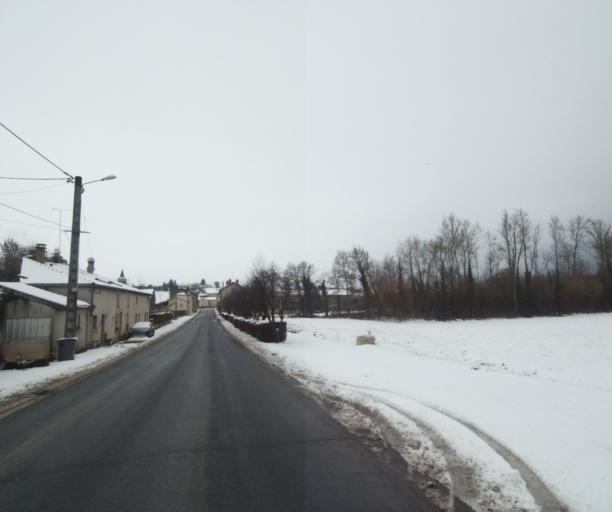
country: FR
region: Champagne-Ardenne
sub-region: Departement de la Haute-Marne
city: Wassy
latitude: 48.4740
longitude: 4.9709
